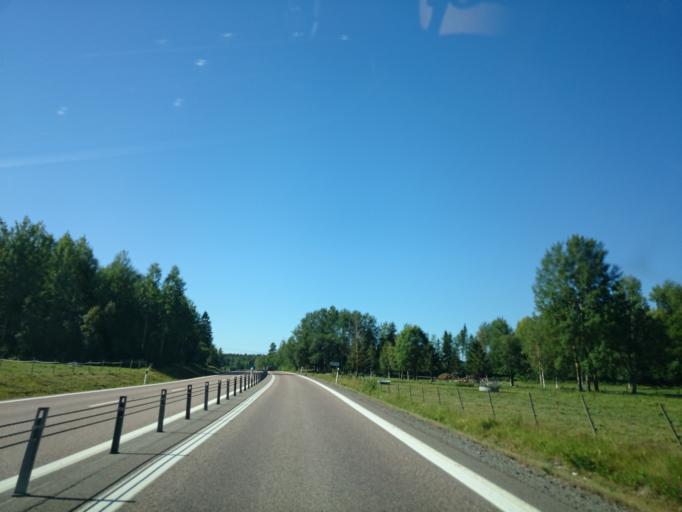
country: SE
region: Gaevleborg
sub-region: Hudiksvalls Kommun
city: Hudiksvall
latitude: 61.7496
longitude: 17.0792
